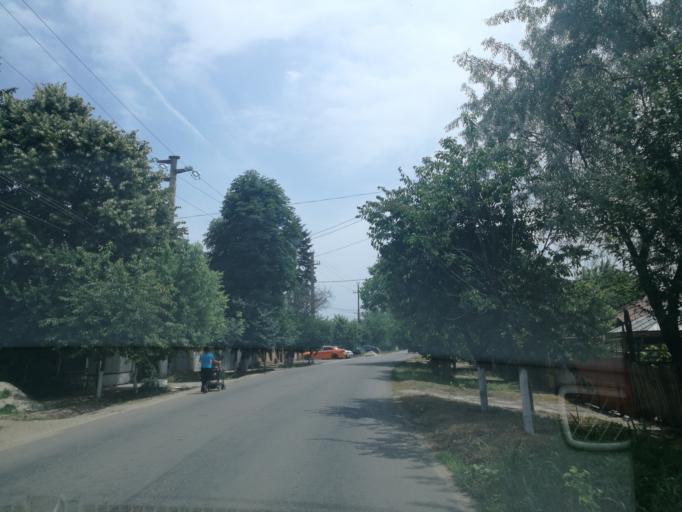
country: RO
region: Ilfov
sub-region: Comuna Vidra
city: Sintesti
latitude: 44.2928
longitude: 26.1289
